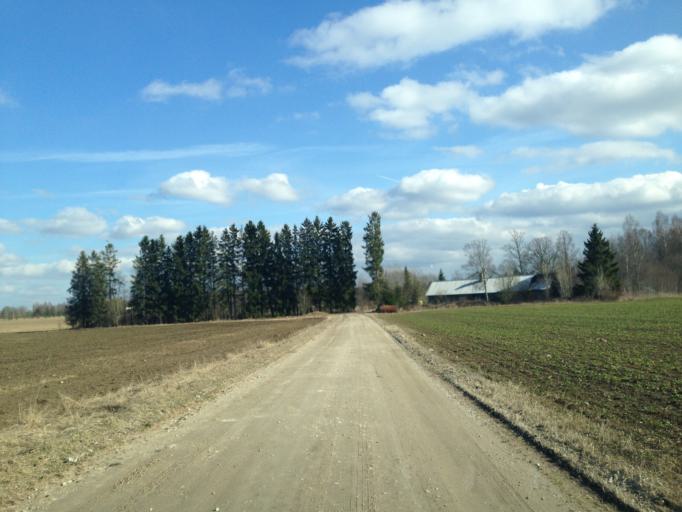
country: EE
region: Harju
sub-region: Keila linn
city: Keila
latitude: 59.1917
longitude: 24.4592
